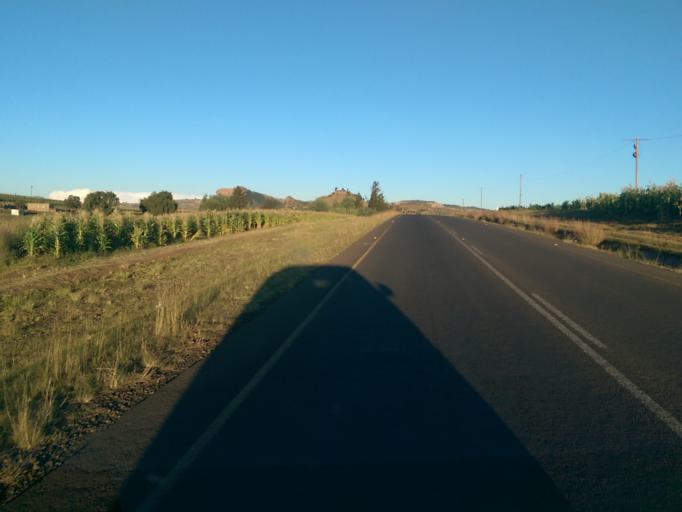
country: LS
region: Maseru
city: Maseru
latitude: -29.4081
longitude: 27.6005
